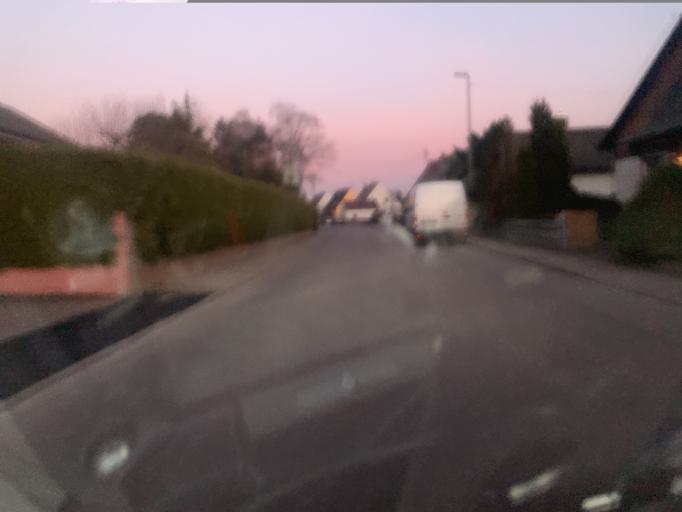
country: DE
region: Bavaria
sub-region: Swabia
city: Dasing
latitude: 48.3854
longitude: 11.0383
